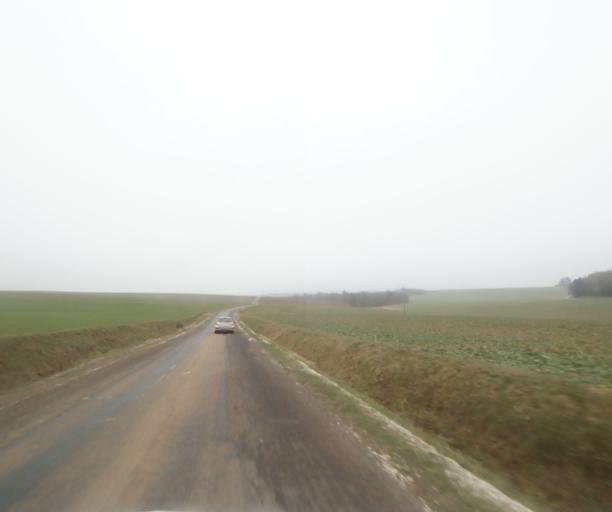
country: FR
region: Champagne-Ardenne
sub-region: Departement de la Haute-Marne
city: Bienville
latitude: 48.5358
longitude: 5.0570
